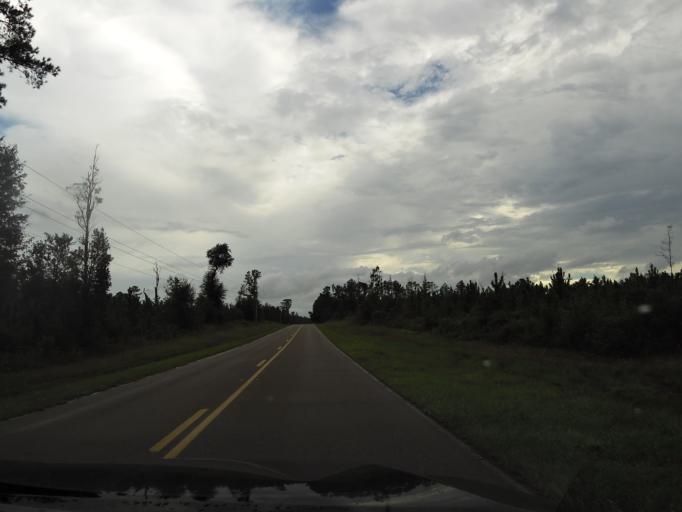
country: US
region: Florida
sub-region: Duval County
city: Baldwin
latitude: 30.4810
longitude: -81.9984
